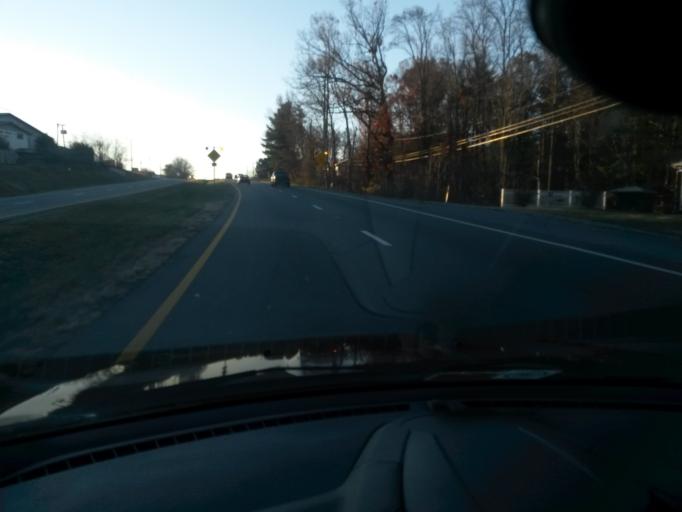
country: US
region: Virginia
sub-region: Franklin County
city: Rocky Mount
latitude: 37.0485
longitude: -79.8808
